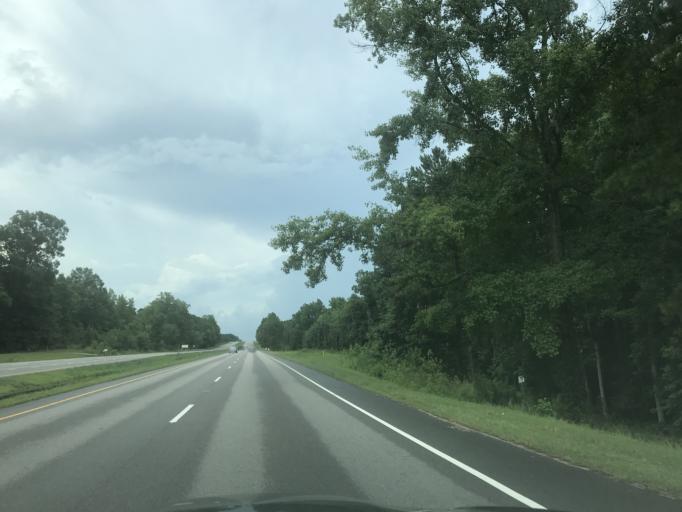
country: US
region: North Carolina
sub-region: Johnston County
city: Clayton
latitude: 35.6809
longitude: -78.5315
